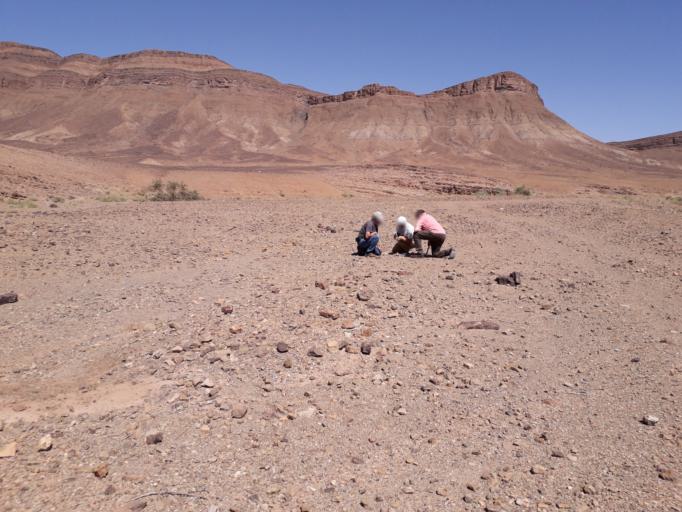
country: MA
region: Meknes-Tafilalet
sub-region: Errachidia
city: Alnif
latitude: 31.0815
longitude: -5.1561
